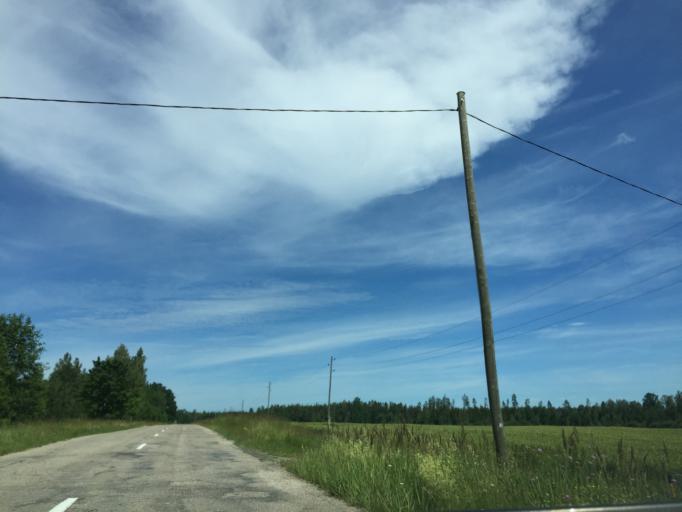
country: LV
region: Dundaga
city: Dundaga
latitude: 57.5554
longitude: 22.3198
